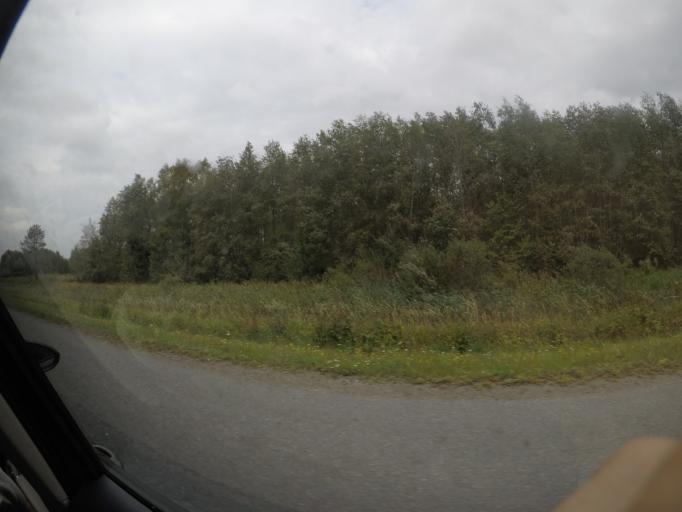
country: FI
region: Haeme
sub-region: Haemeenlinna
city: Parola
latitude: 61.0377
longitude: 24.4063
